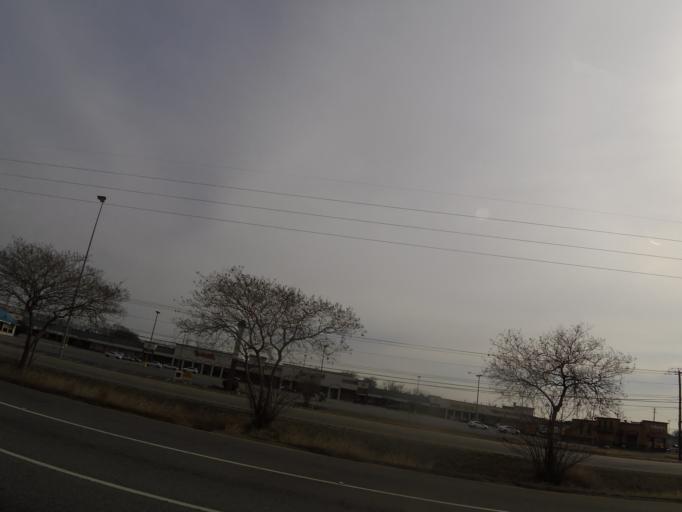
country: US
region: Alabama
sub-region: Montgomery County
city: Montgomery
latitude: 32.3451
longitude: -86.2236
